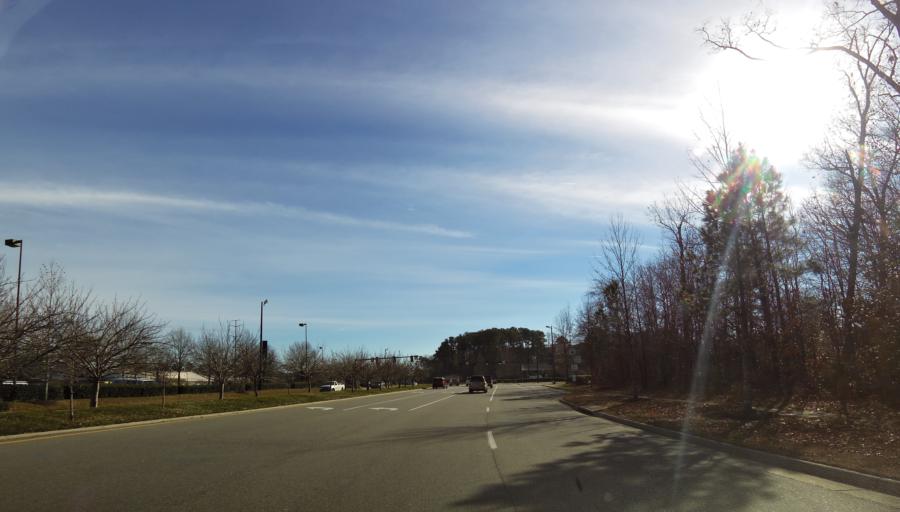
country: US
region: Virginia
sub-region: City of Hampton
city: Hampton
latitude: 37.0371
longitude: -76.3983
